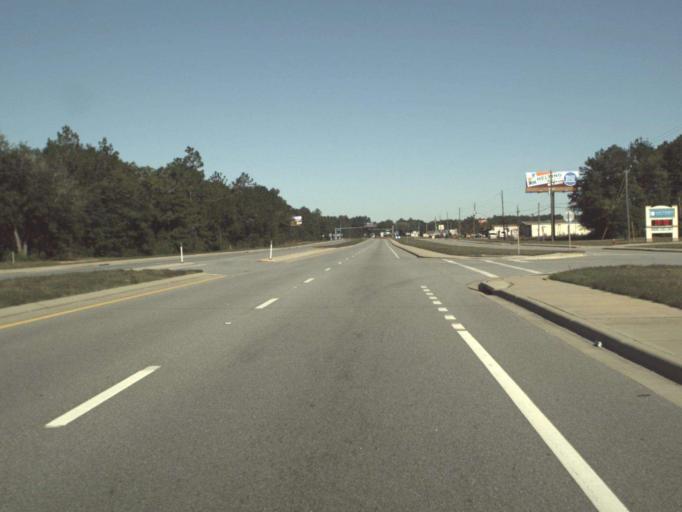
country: US
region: Florida
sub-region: Santa Rosa County
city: Bagdad
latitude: 30.5803
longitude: -87.0862
